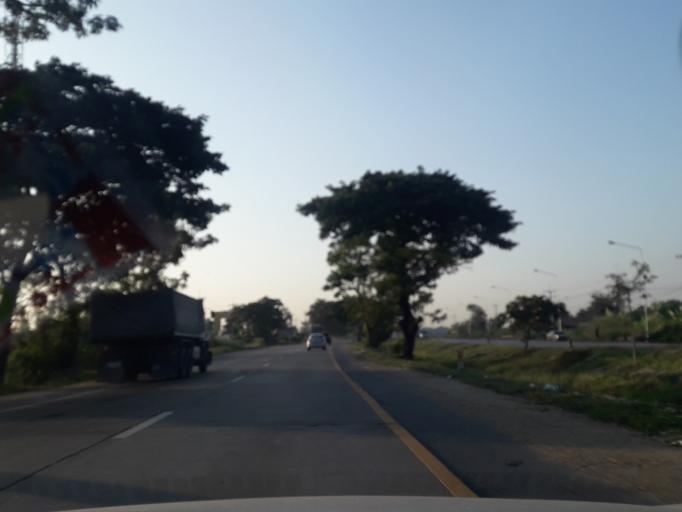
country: TH
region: Phra Nakhon Si Ayutthaya
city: Bang Pa-in
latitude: 14.2623
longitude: 100.5338
